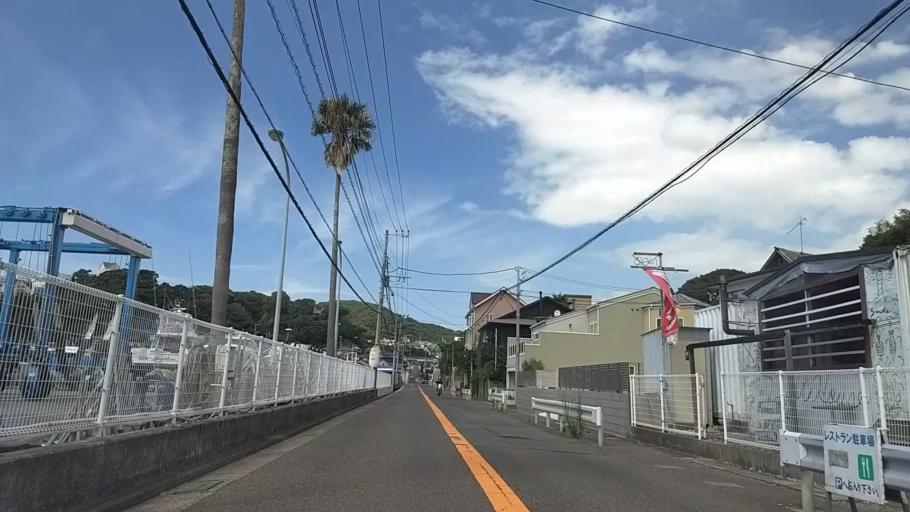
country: JP
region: Kanagawa
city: Hayama
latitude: 35.2302
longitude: 139.6038
